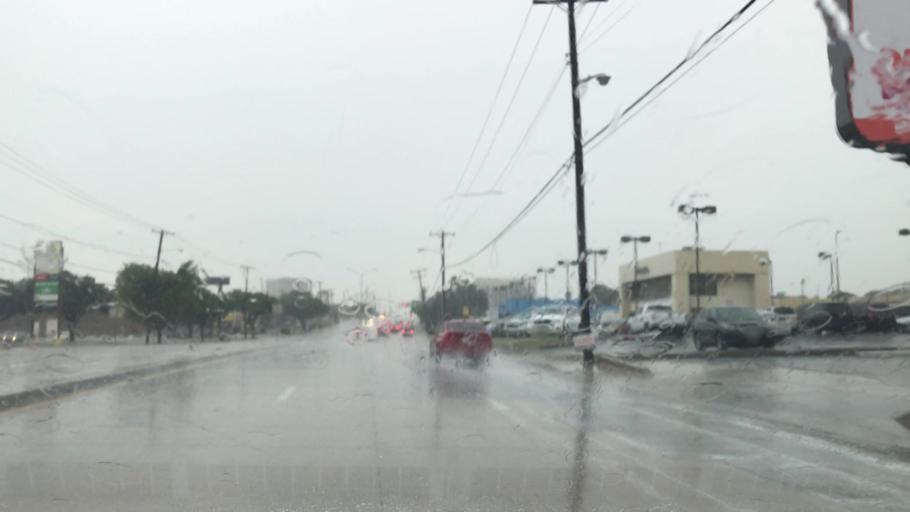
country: US
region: Texas
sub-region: Dallas County
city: Addison
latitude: 32.9324
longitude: -96.8037
